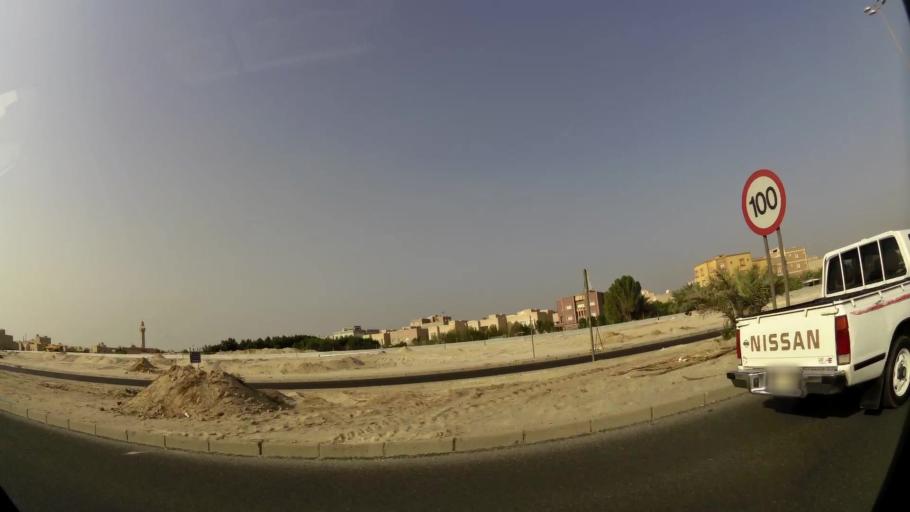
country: KW
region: Al Asimah
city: Ar Rabiyah
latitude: 29.2956
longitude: 47.8673
